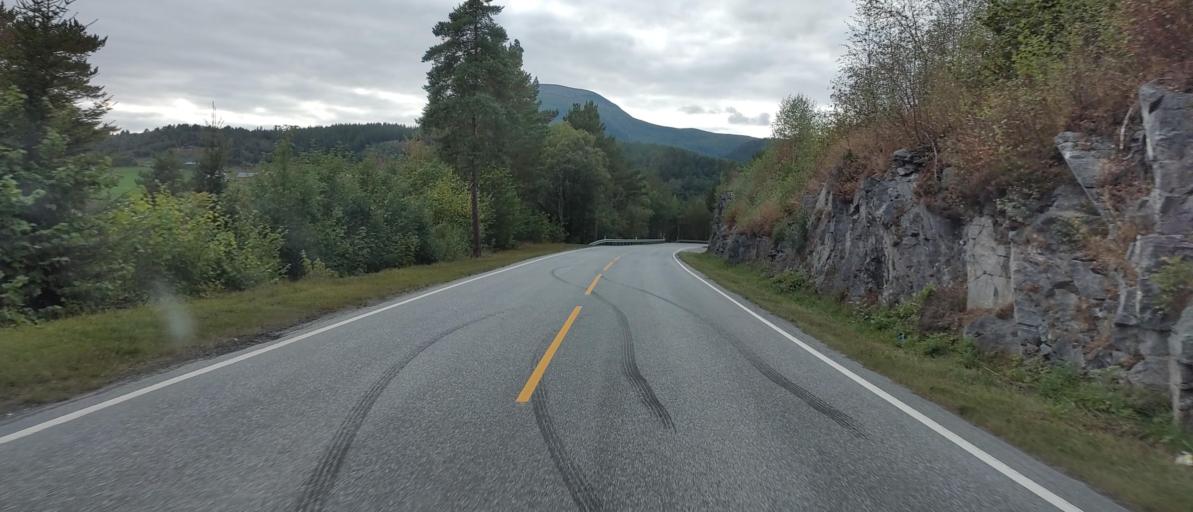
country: NO
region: More og Romsdal
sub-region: Rauma
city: Andalsnes
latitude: 62.5822
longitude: 7.5429
